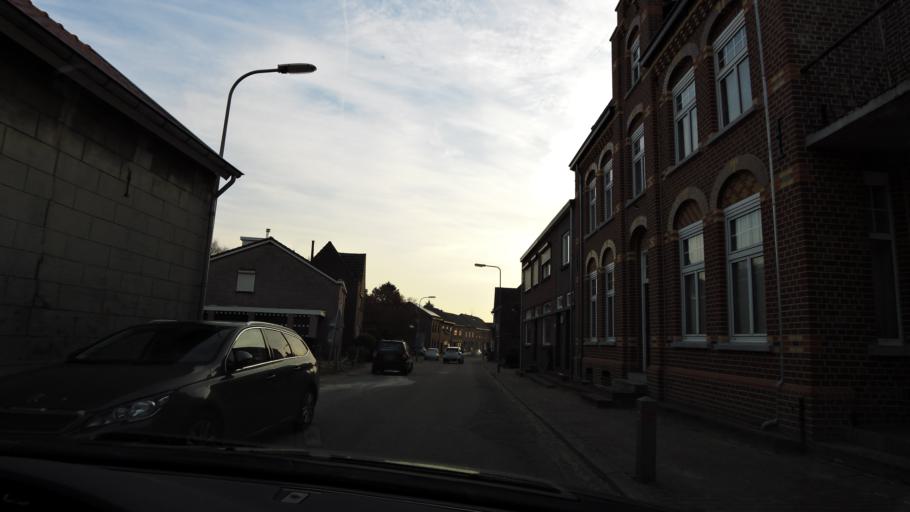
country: NL
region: Limburg
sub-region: Gemeente Onderbanken
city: Merkelbeek
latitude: 50.9512
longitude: 5.9463
